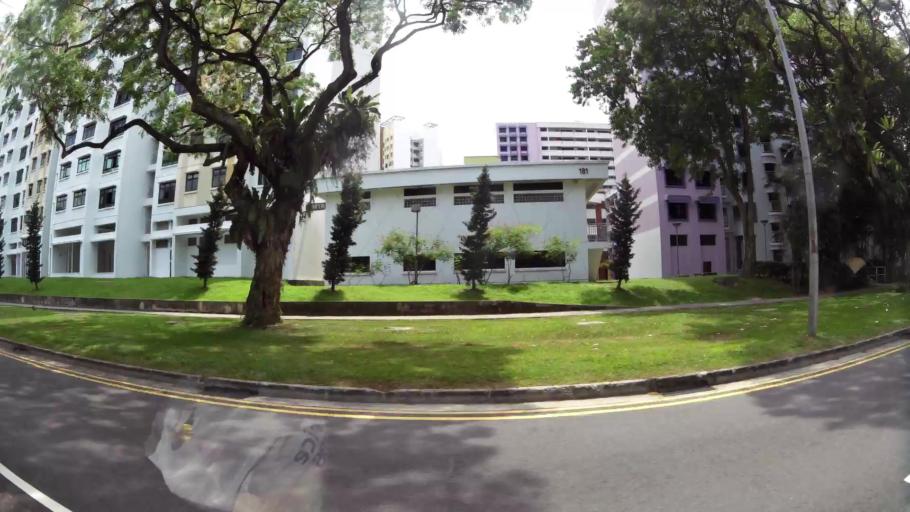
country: MY
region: Johor
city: Johor Bahru
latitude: 1.3486
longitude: 103.7076
